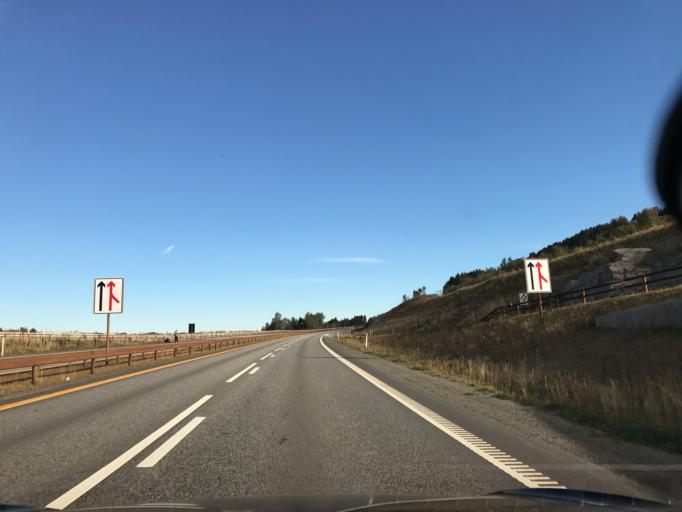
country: NO
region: Hedmark
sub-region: Stange
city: Stange
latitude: 60.5639
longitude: 11.2561
